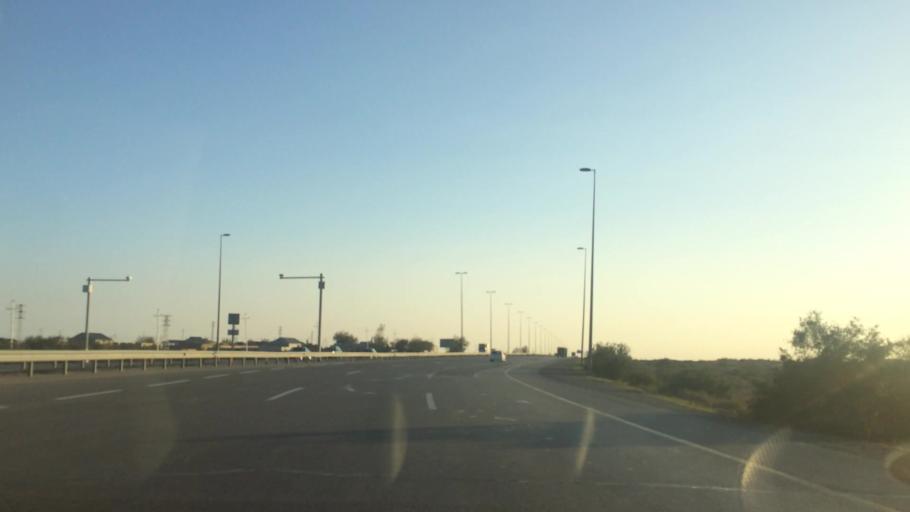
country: AZ
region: Baki
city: Qobustan
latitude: 39.9909
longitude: 49.4300
